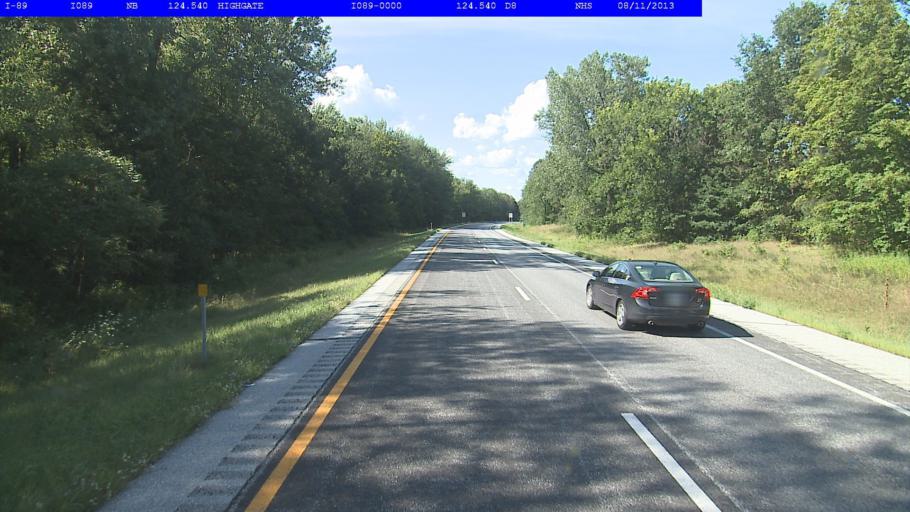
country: US
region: Vermont
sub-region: Franklin County
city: Swanton
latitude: 44.9386
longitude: -73.1141
